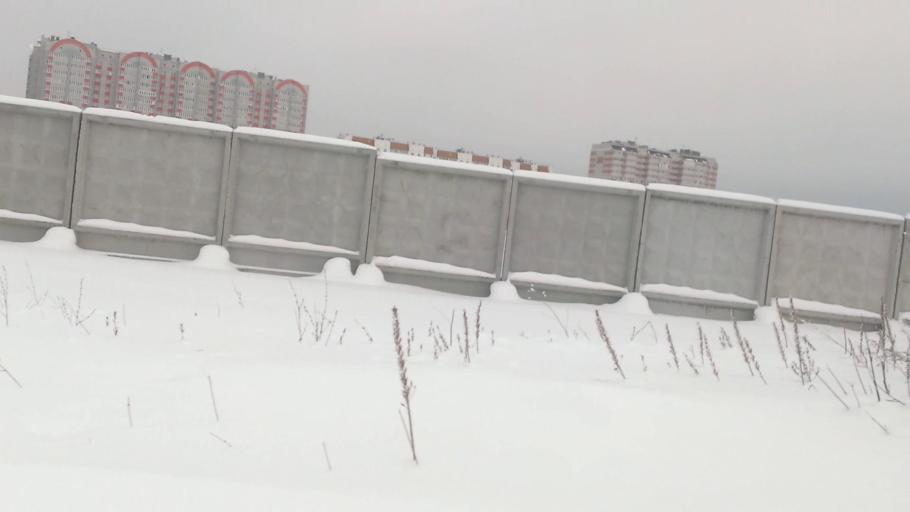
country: RU
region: Altai Krai
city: Novosilikatnyy
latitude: 53.3516
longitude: 83.6603
